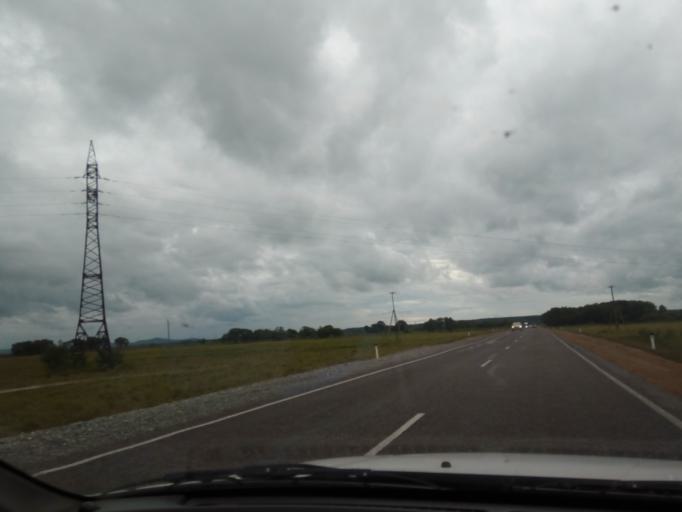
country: RU
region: Primorskiy
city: Dal'nerechensk
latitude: 45.9095
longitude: 133.7604
